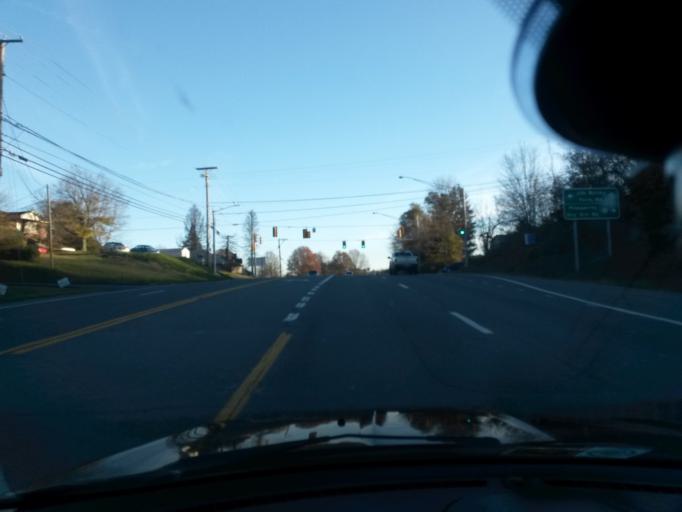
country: US
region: West Virginia
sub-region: Raleigh County
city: Prosperity
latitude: 37.8435
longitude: -81.1940
